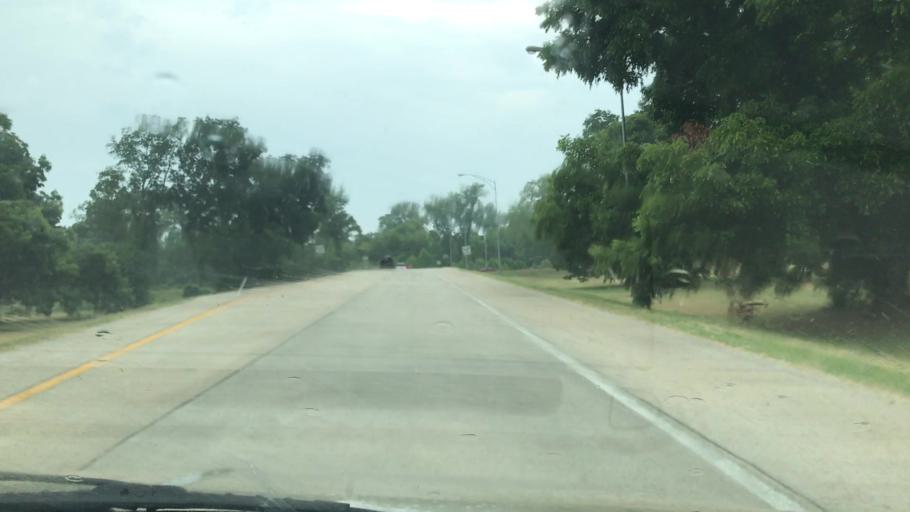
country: US
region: Louisiana
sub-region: Bossier Parish
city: Bossier City
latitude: 32.4576
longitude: -93.6732
